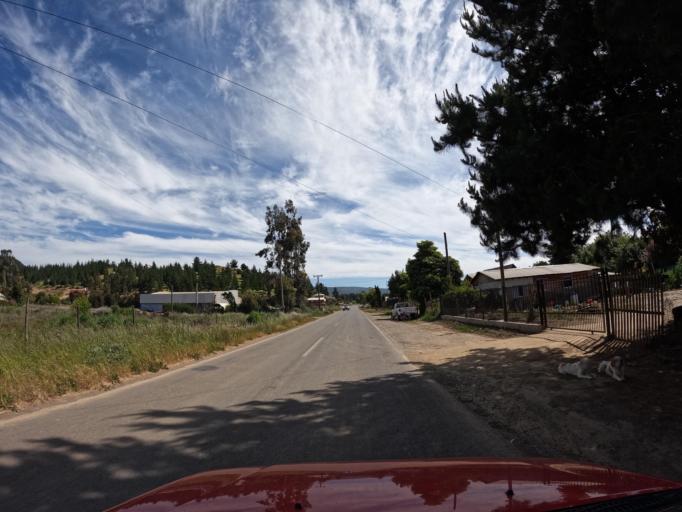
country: CL
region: Maule
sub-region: Provincia de Talca
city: Constitucion
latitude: -35.0282
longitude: -72.0488
